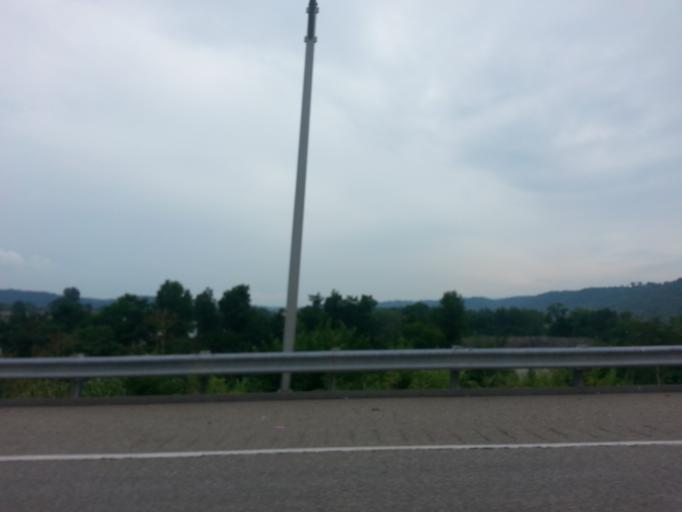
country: US
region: Ohio
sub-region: Brown County
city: Aberdeen
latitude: 38.6856
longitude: -83.7778
